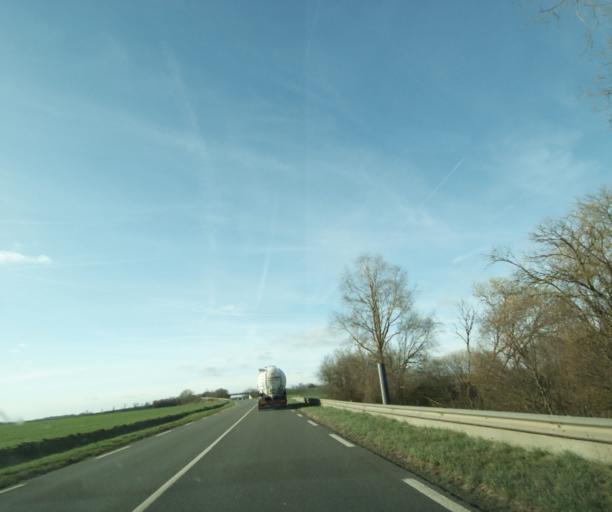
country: FR
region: Ile-de-France
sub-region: Departement des Yvelines
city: Ablis
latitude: 48.5063
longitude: 1.8357
